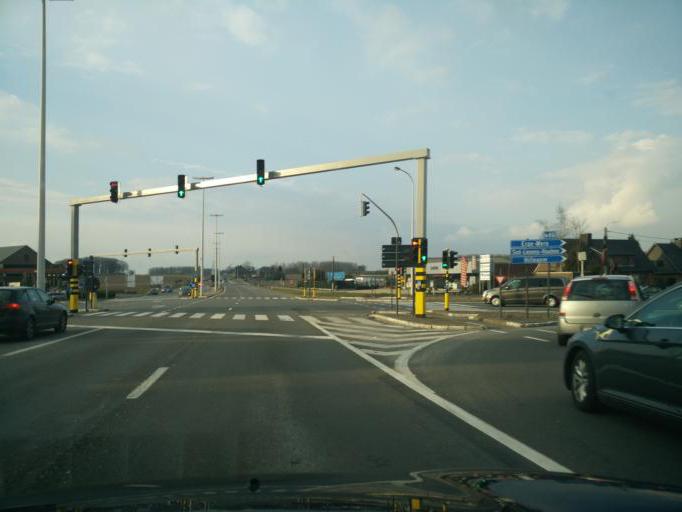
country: BE
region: Flanders
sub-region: Provincie Oost-Vlaanderen
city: Perre
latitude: 50.8980
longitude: 3.8295
